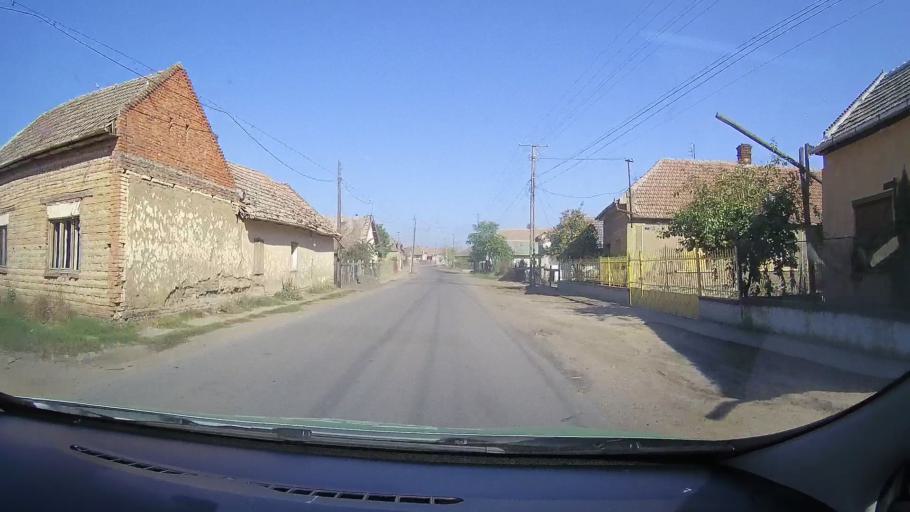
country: RO
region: Satu Mare
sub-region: Comuna Ciumesti
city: Ciumesti
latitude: 47.6560
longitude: 22.3337
